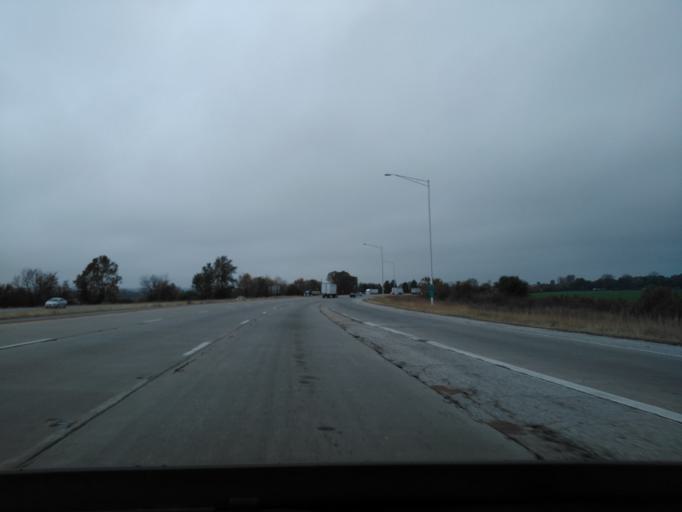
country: US
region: Illinois
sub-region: Saint Clair County
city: Caseyville
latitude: 38.6546
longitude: -90.0330
